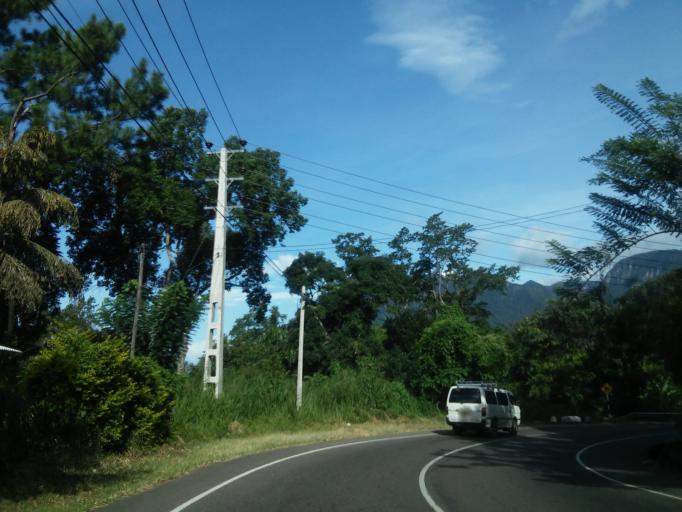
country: LK
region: Uva
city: Haputale
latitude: 6.7641
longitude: 80.8711
